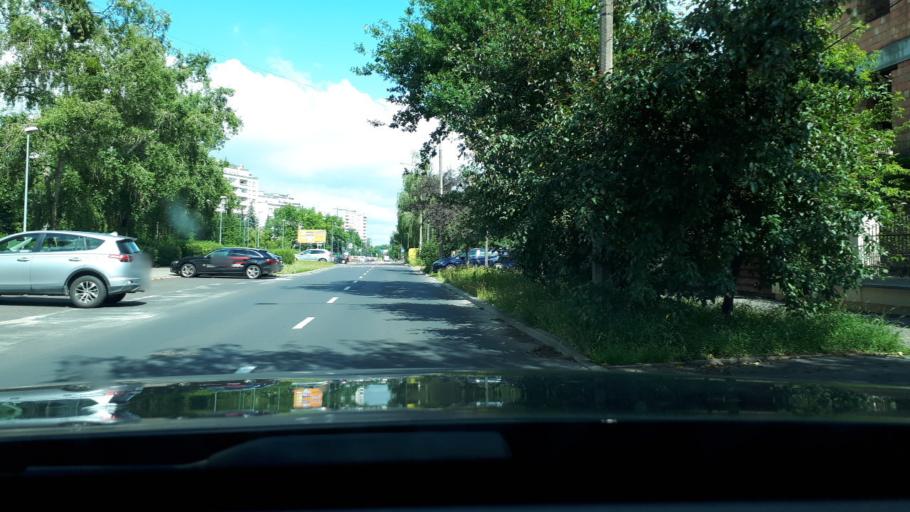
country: PL
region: Masovian Voivodeship
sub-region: Warszawa
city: Wilanow
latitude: 52.1709
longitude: 21.0751
